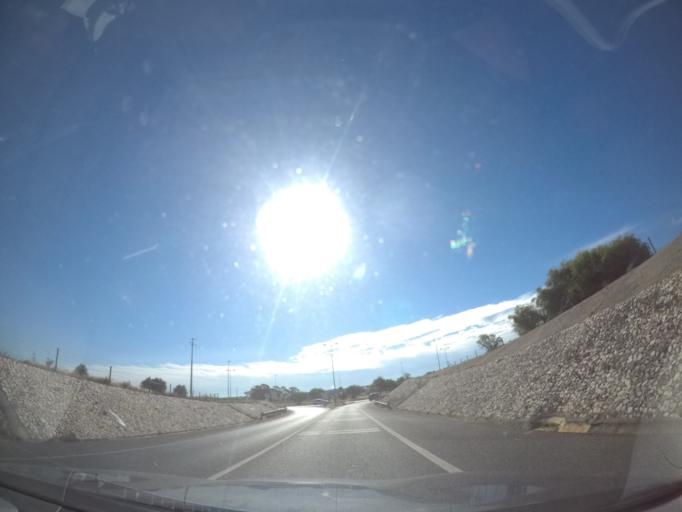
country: PT
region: Faro
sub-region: Lagos
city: Lagos
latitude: 37.1396
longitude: -8.6642
